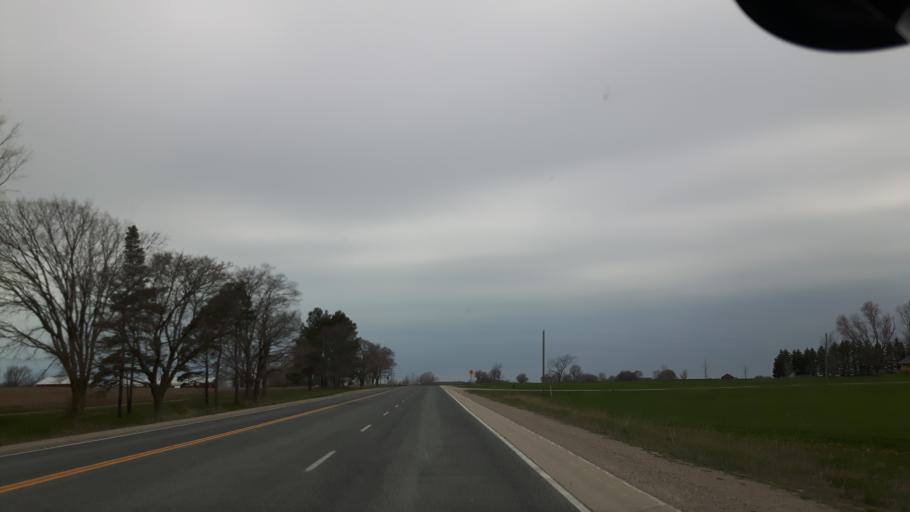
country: CA
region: Ontario
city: Goderich
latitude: 43.6517
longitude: -81.6097
